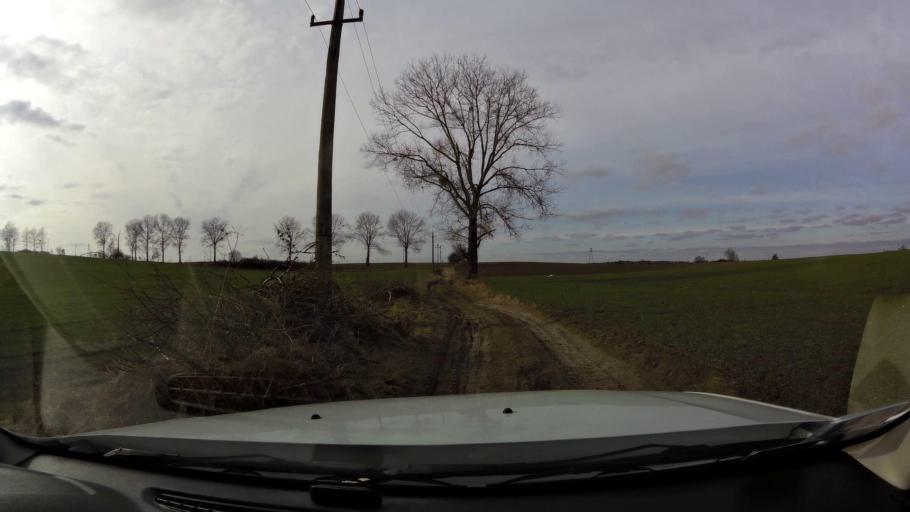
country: PL
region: West Pomeranian Voivodeship
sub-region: Powiat drawski
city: Drawsko Pomorskie
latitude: 53.5252
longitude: 15.7625
